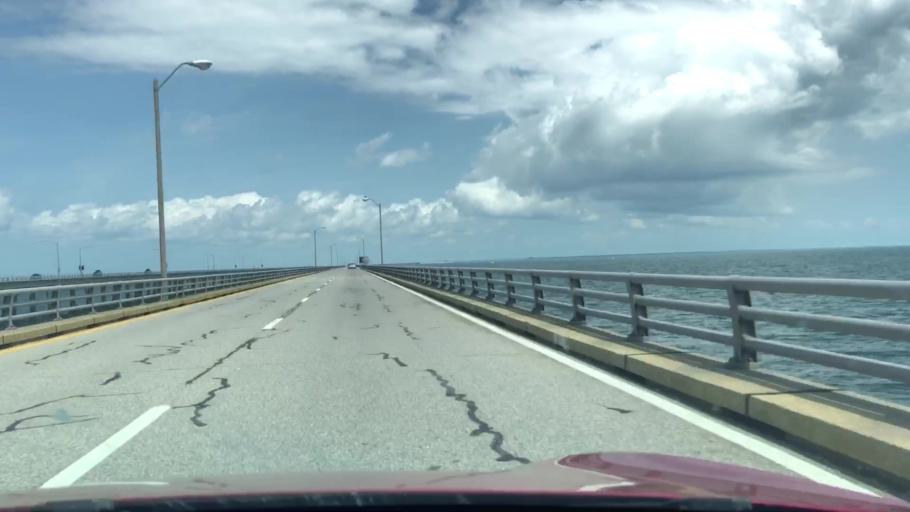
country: US
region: Virginia
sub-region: City of Virginia Beach
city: Virginia Beach
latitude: 36.9939
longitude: -76.1011
